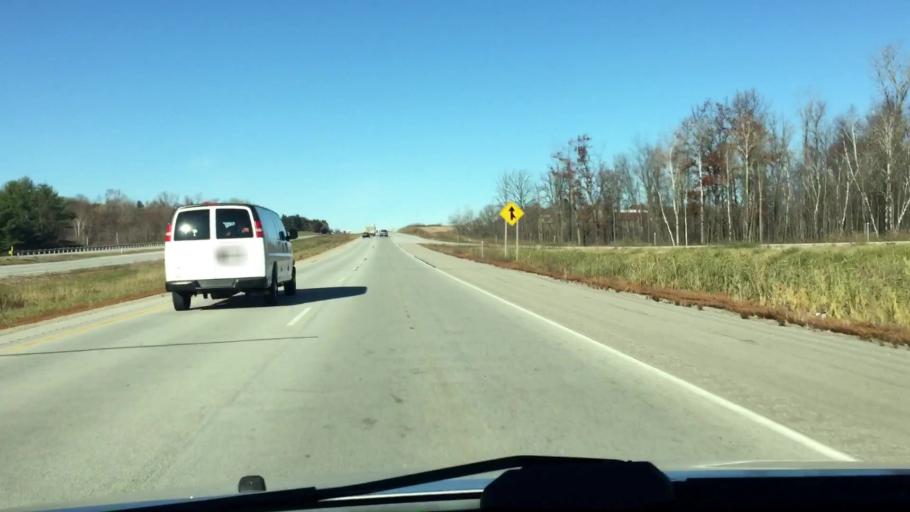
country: US
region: Wisconsin
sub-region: Brown County
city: Howard
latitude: 44.5616
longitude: -88.1329
